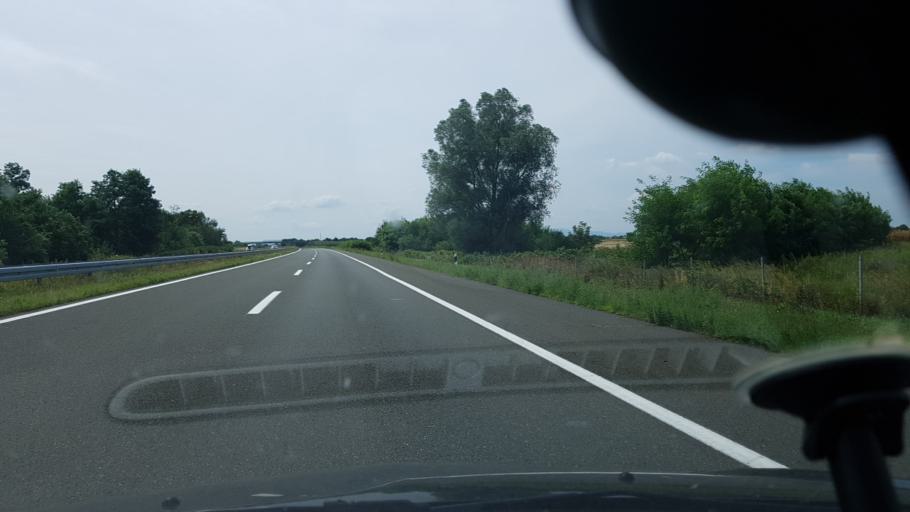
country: HR
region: Medimurska
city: Palovec
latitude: 46.3938
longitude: 16.5647
